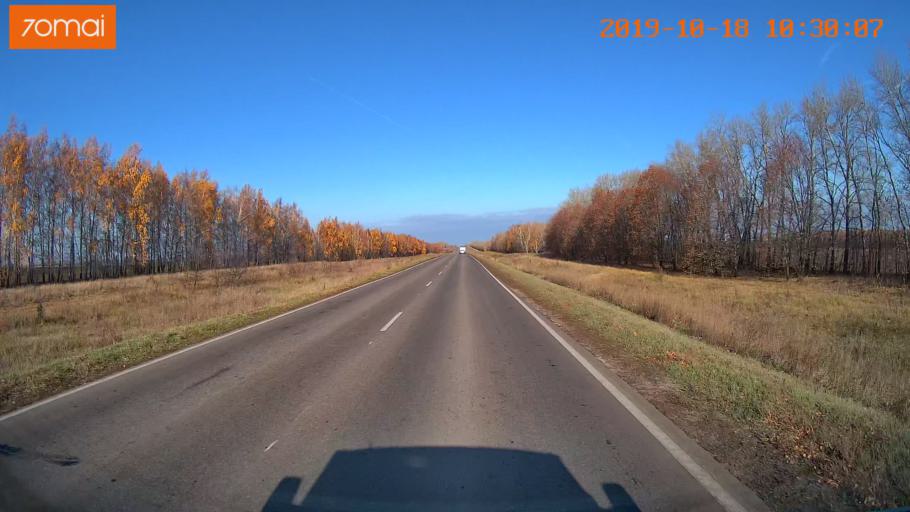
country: RU
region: Tula
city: Kurkino
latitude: 53.4610
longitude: 38.6481
